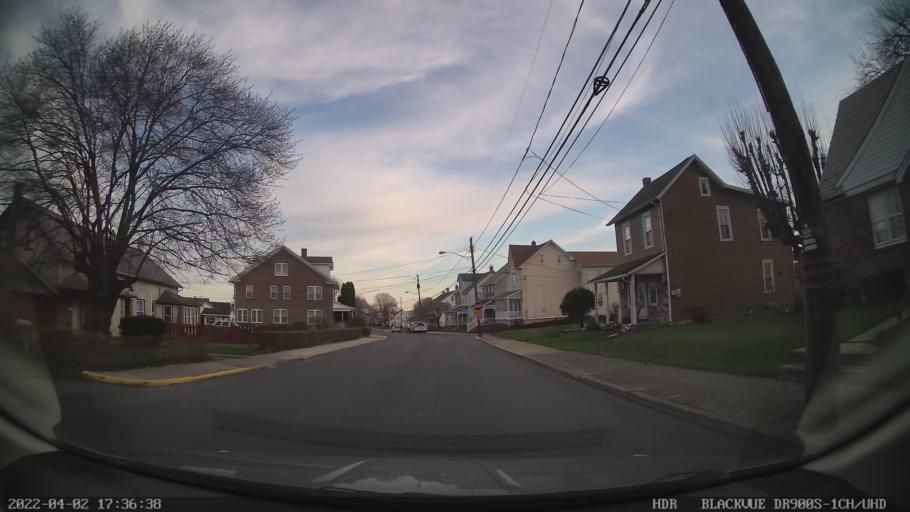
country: US
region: Pennsylvania
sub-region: Northampton County
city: Northampton
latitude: 40.6951
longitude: -75.4972
